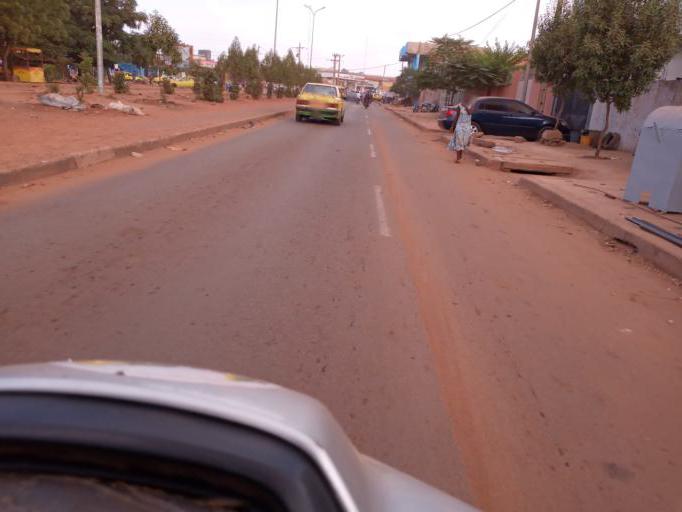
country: ML
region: Bamako
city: Bamako
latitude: 12.5975
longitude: -7.9393
